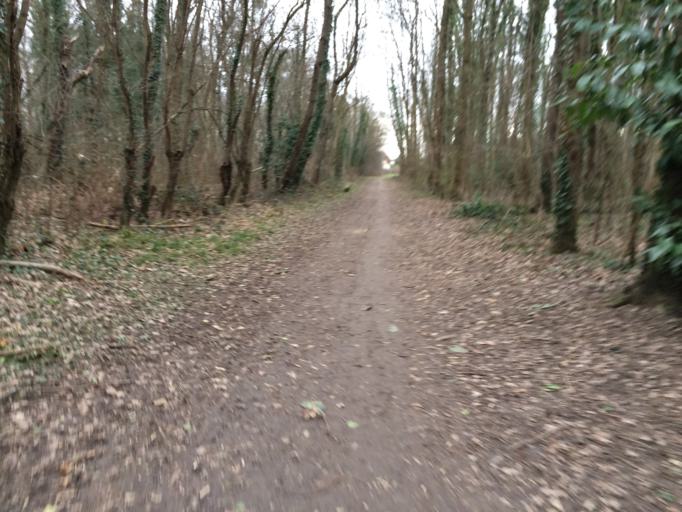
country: FR
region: Ile-de-France
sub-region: Departement de l'Essonne
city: Villebon-sur-Yvette
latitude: 48.7146
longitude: 2.2278
